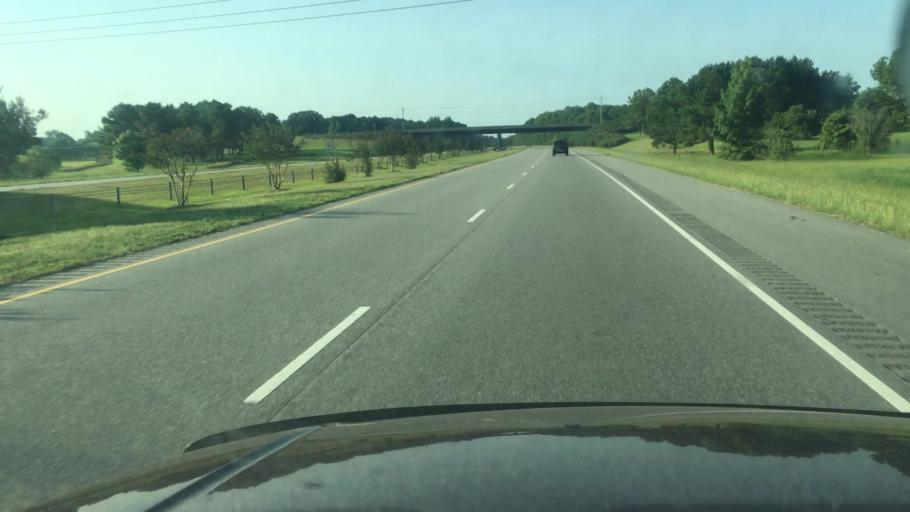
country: US
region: North Carolina
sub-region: Cumberland County
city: Fayetteville
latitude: 35.0124
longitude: -78.8699
